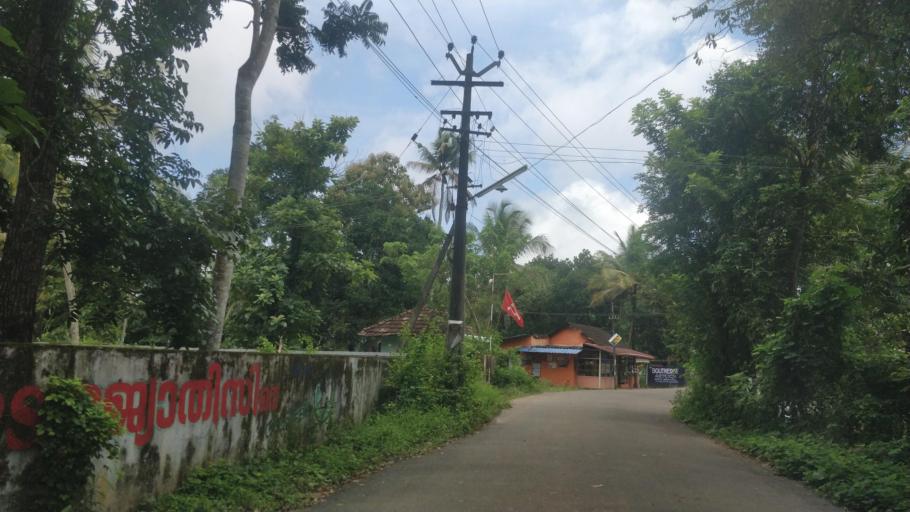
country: IN
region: Kerala
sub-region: Alappuzha
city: Shertallai
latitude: 9.6637
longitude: 76.3766
